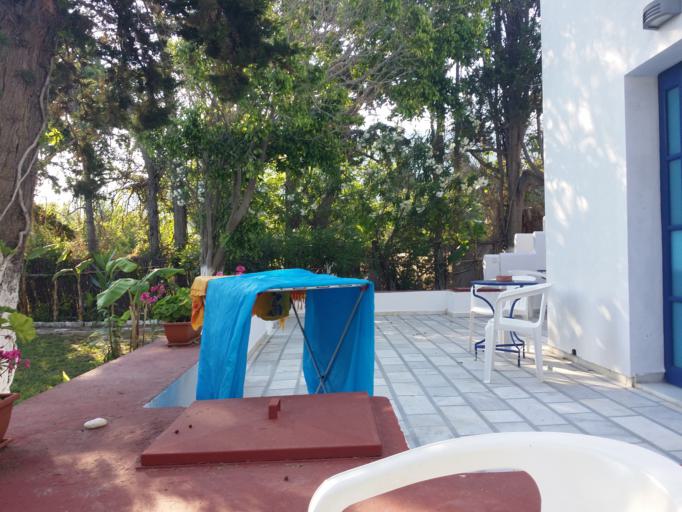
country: GR
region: South Aegean
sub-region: Nomos Kykladon
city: Paros
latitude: 37.0809
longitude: 25.1468
